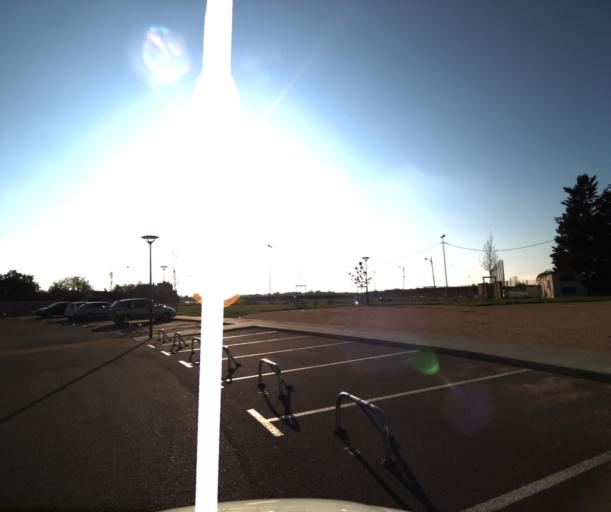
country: FR
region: Midi-Pyrenees
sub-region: Departement de la Haute-Garonne
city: Colomiers
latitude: 43.6237
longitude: 1.3222
